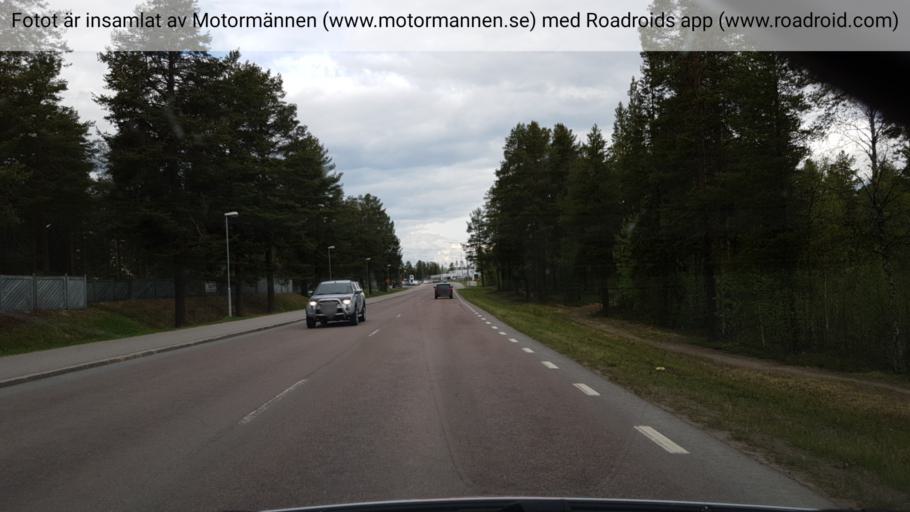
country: SE
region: Norrbotten
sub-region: Arvidsjaurs Kommun
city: Arvidsjaur
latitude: 65.5830
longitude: 19.2025
